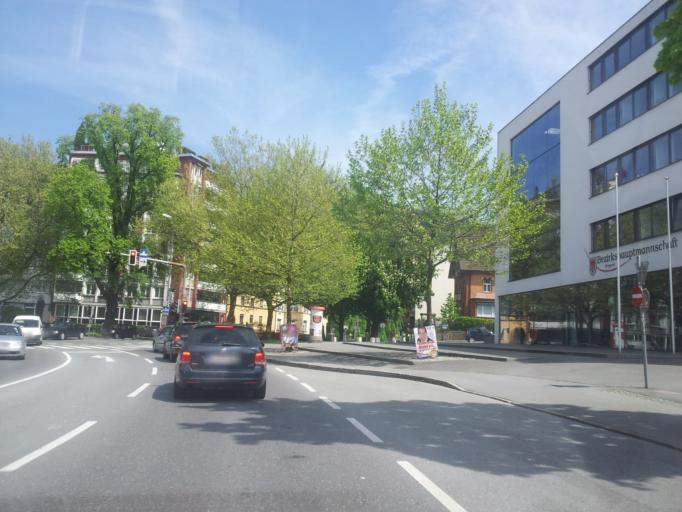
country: AT
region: Vorarlberg
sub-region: Politischer Bezirk Bregenz
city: Bregenz
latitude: 47.5019
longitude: 9.7401
